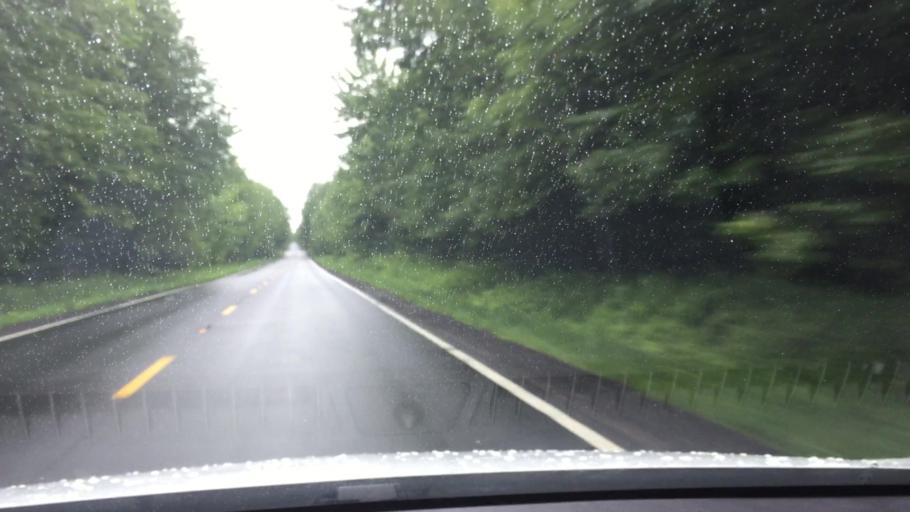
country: US
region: Massachusetts
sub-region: Berkshire County
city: Hinsdale
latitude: 42.3799
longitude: -73.1532
